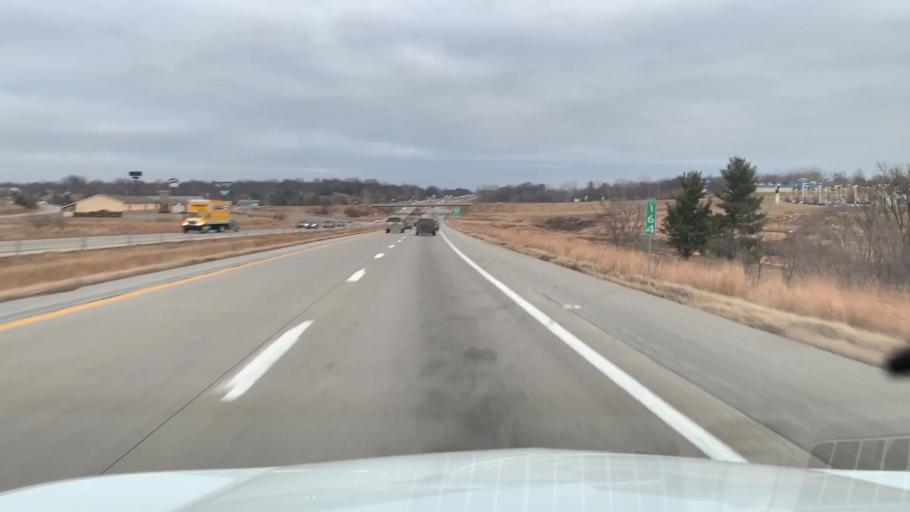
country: US
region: Iowa
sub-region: Jasper County
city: Newton
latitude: 41.6826
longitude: -93.0838
